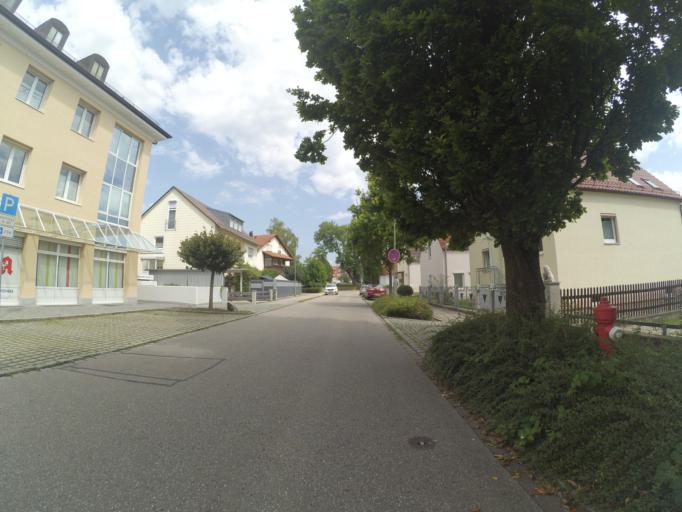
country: DE
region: Bavaria
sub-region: Swabia
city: Buchloe
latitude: 48.0352
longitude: 10.7247
